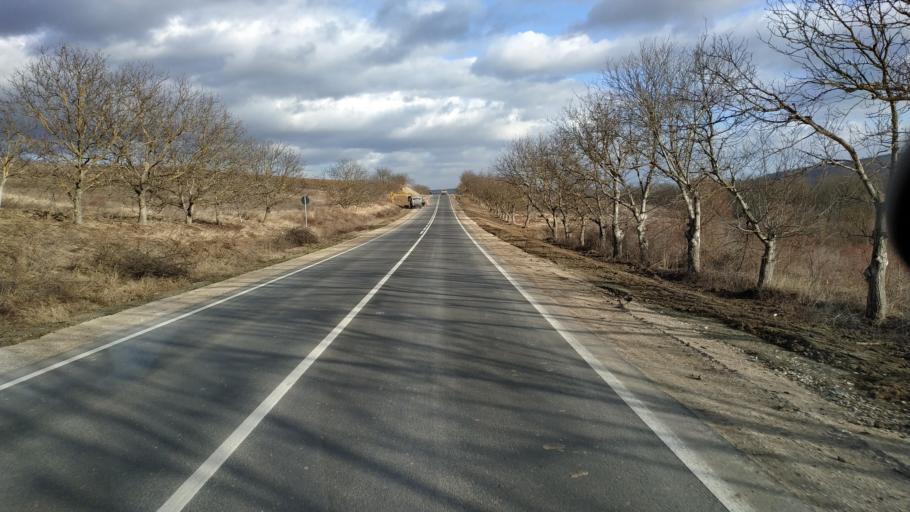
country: MD
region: Calarasi
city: Calarasi
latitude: 47.2964
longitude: 28.1571
